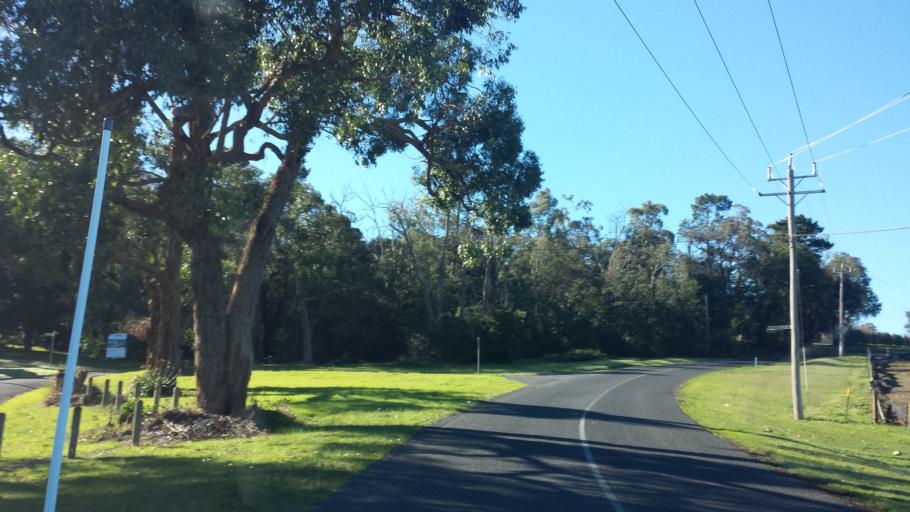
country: AU
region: Victoria
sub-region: Yarra Ranges
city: Healesville
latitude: -37.6695
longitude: 145.5124
